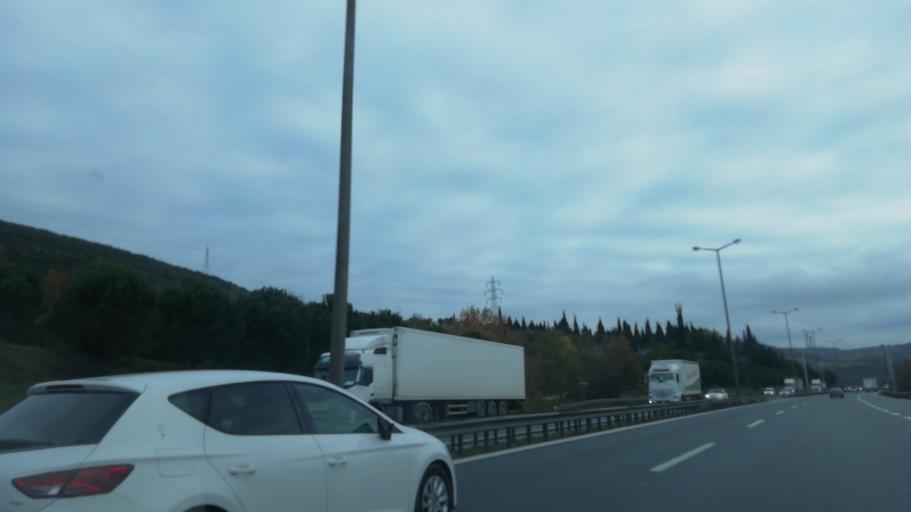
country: TR
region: Kocaeli
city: Izmit
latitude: 40.7764
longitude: 29.8756
